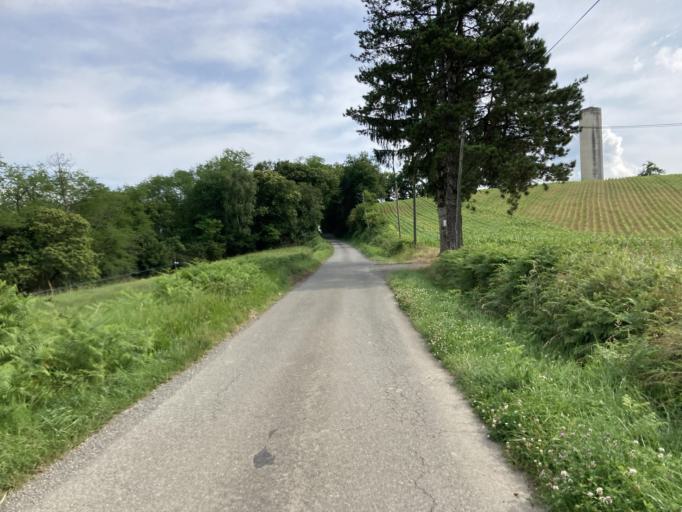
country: FR
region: Aquitaine
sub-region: Departement des Pyrenees-Atlantiques
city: Ledeuix
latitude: 43.2701
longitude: -0.6053
